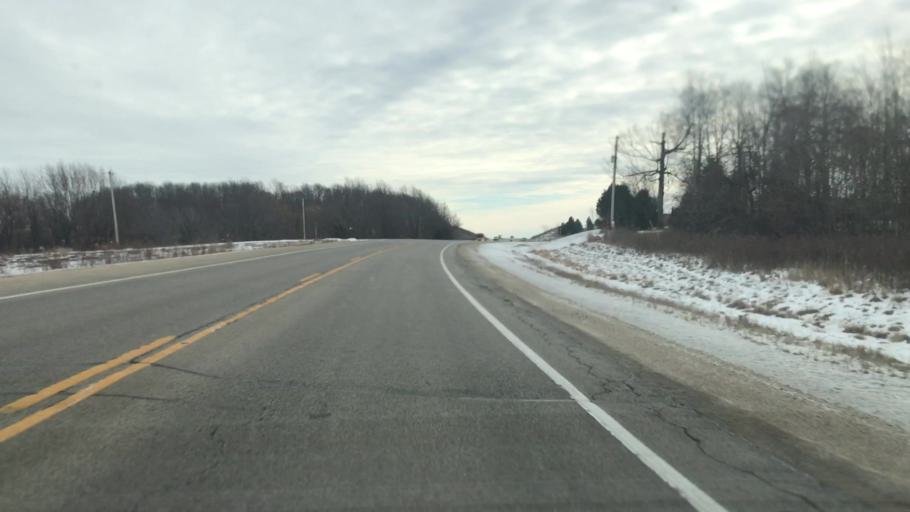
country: US
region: Wisconsin
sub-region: Dodge County
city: Theresa
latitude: 43.4397
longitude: -88.4815
